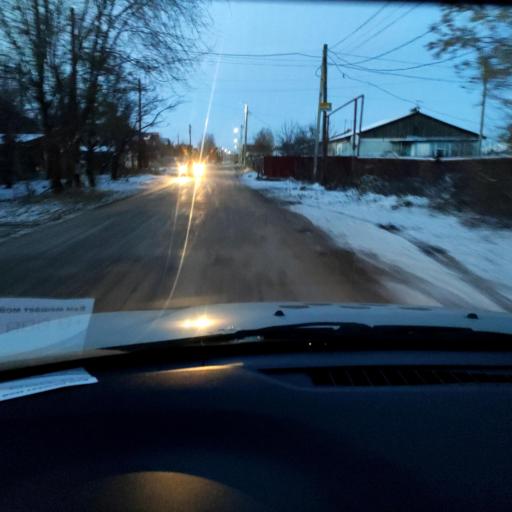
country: RU
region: Samara
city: Tol'yatti
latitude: 53.5645
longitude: 49.3898
